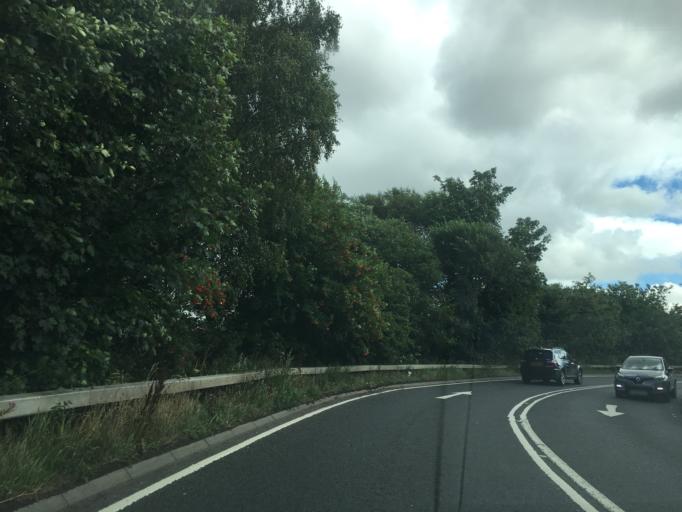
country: GB
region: Scotland
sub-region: Renfrewshire
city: Inchinnan
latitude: 55.8602
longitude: -4.4501
